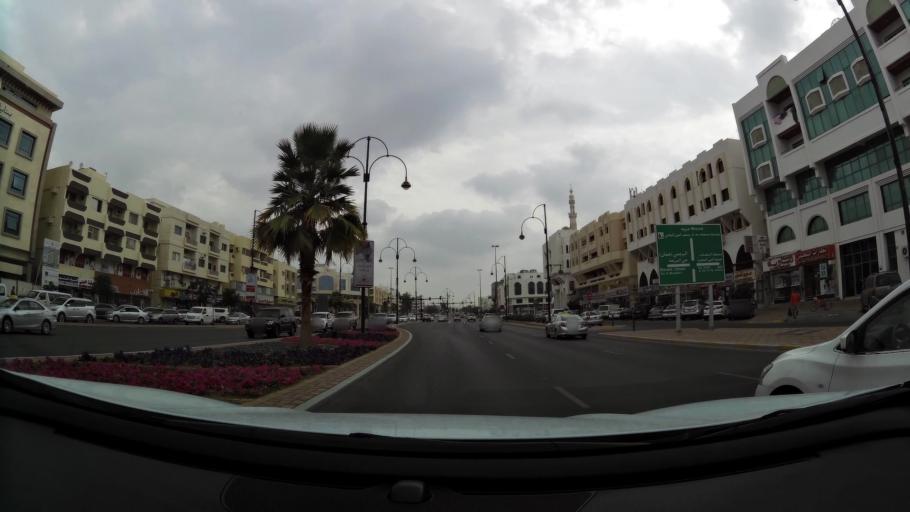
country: AE
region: Abu Dhabi
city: Al Ain
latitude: 24.2221
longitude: 55.7690
